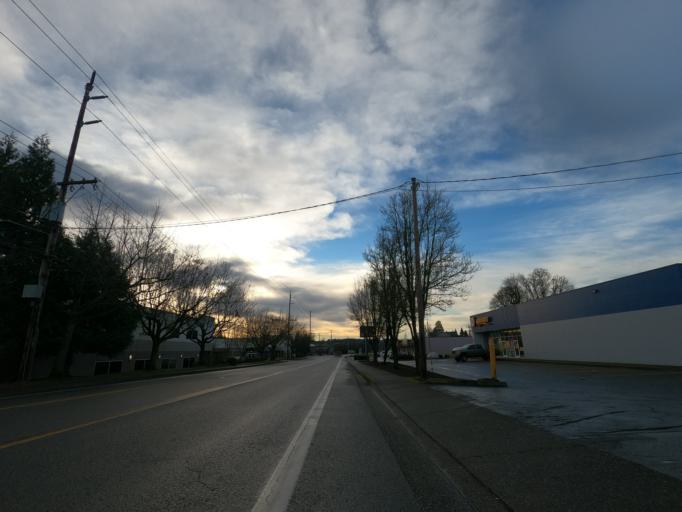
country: US
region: Oregon
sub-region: Clackamas County
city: Clackamas
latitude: 45.4143
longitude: -122.5690
